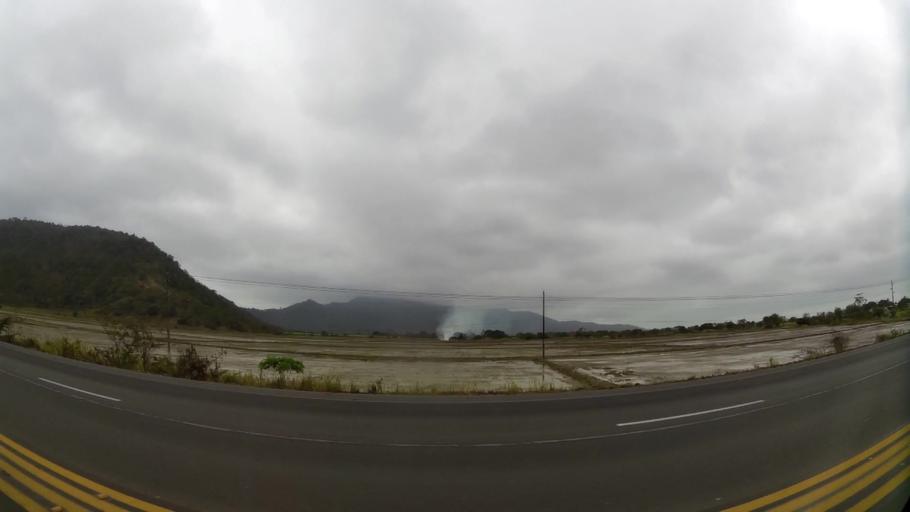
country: EC
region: Guayas
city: Naranjal
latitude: -2.4673
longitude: -79.6232
